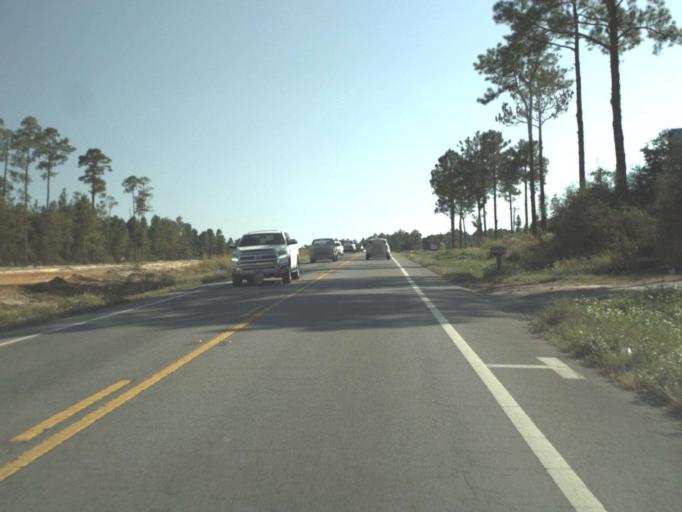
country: US
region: Florida
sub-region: Walton County
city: DeFuniak Springs
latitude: 30.6720
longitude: -86.1229
